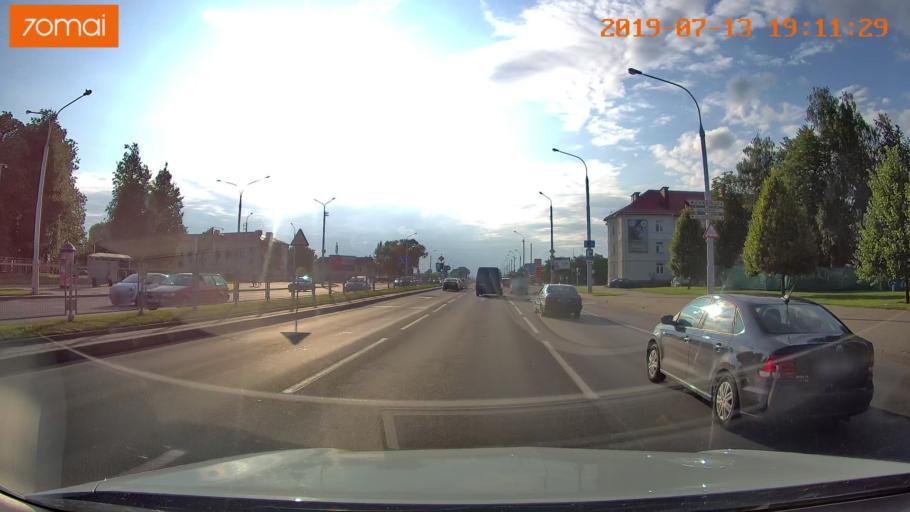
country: BY
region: Minsk
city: Syenitsa
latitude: 53.8740
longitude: 27.5291
